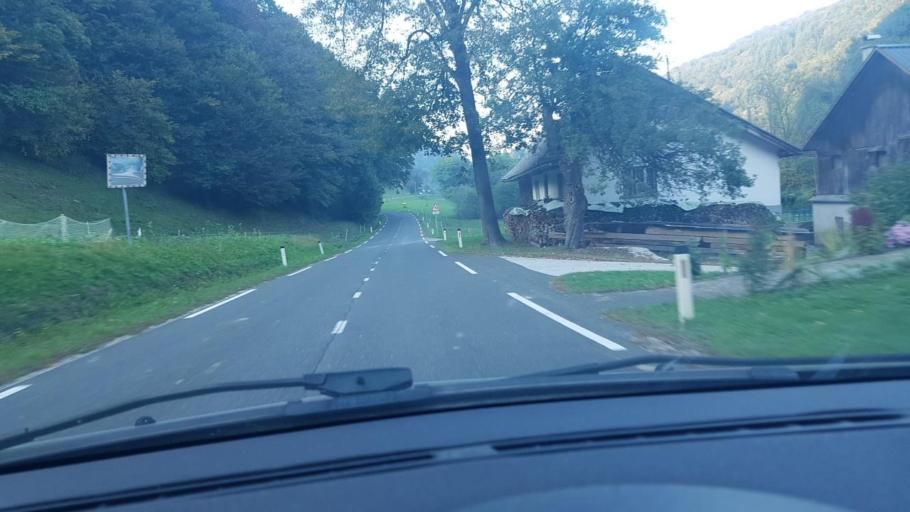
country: SI
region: Makole
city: Makole
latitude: 46.2987
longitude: 15.7185
